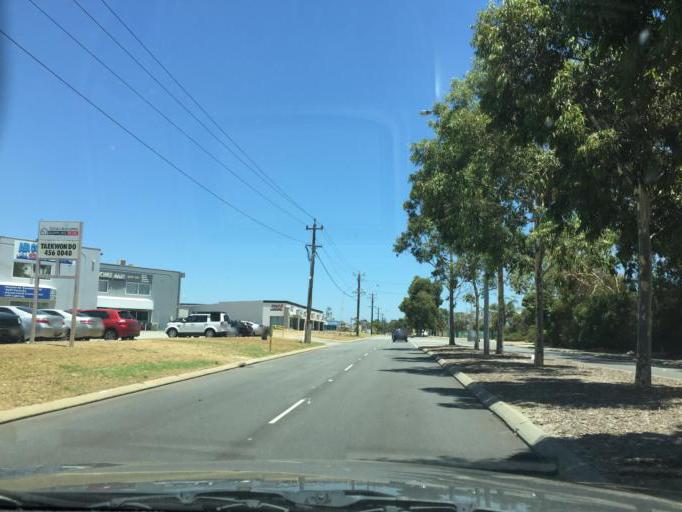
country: AU
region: Western Australia
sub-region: Canning
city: Canning Vale
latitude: -32.0579
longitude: 115.9157
